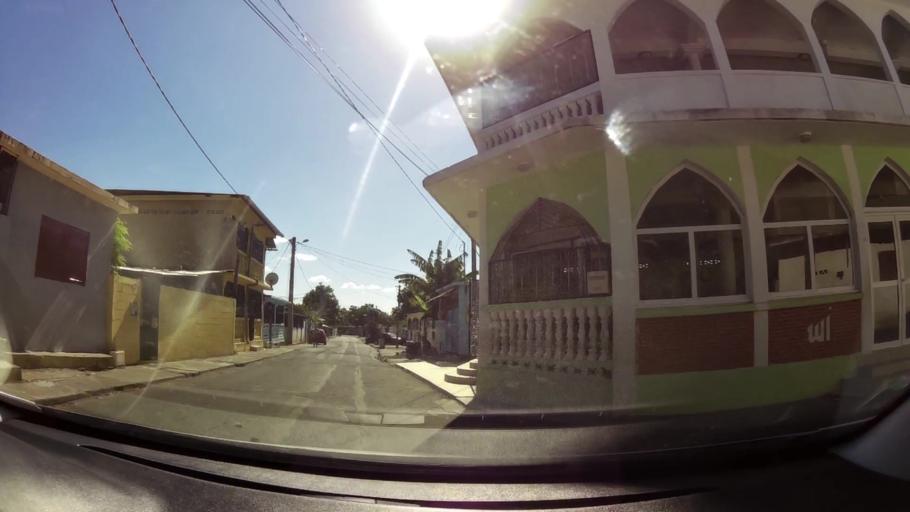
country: YT
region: Pamandzi
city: Pamandzi
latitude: -12.7872
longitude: 45.2775
